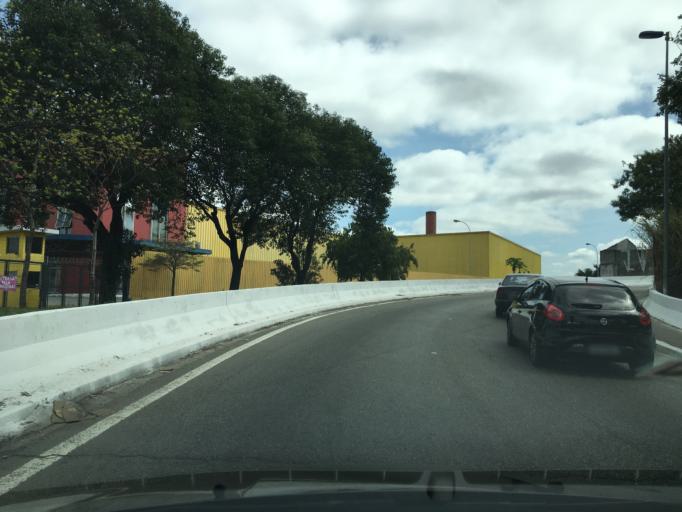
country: BR
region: Sao Paulo
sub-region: Sao Paulo
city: Sao Paulo
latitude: -23.5277
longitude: -46.5864
